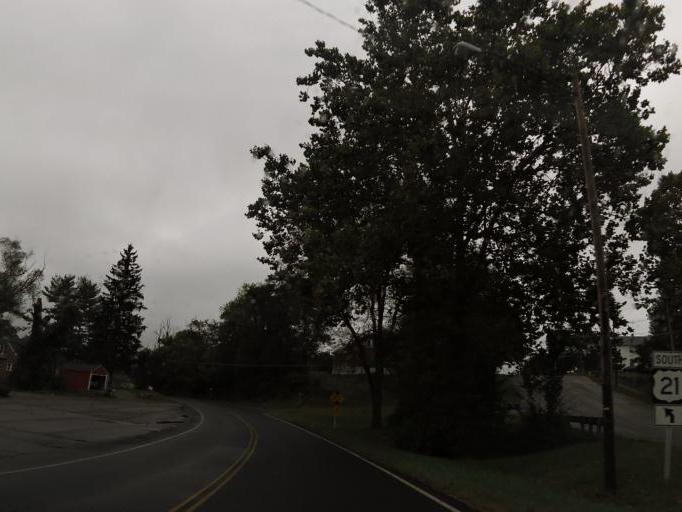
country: US
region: Virginia
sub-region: Wythe County
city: Wytheville
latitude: 36.9406
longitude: -81.0957
